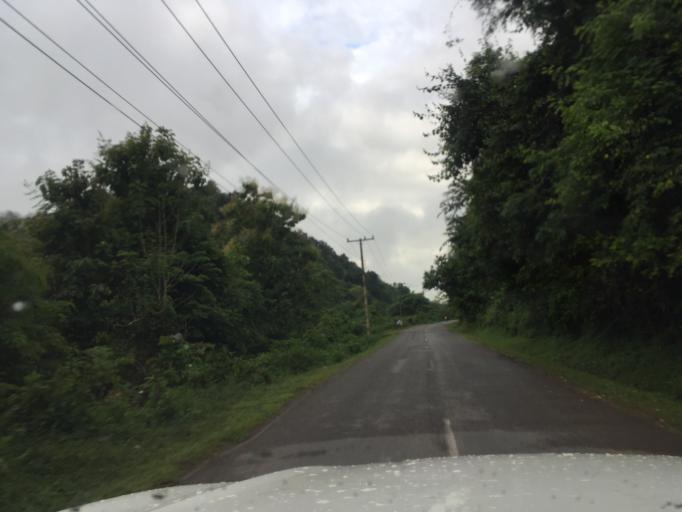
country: LA
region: Oudomxai
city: Muang La
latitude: 20.8665
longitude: 102.1284
